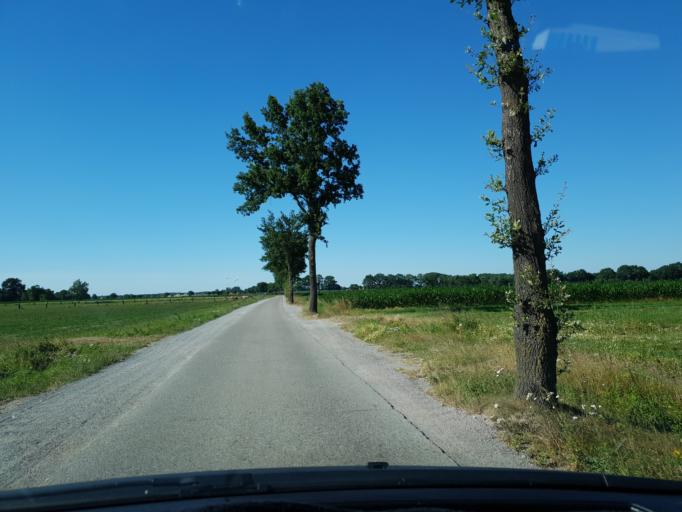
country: BE
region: Flanders
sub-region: Provincie Antwerpen
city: Hoogstraten
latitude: 51.4238
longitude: 4.7230
